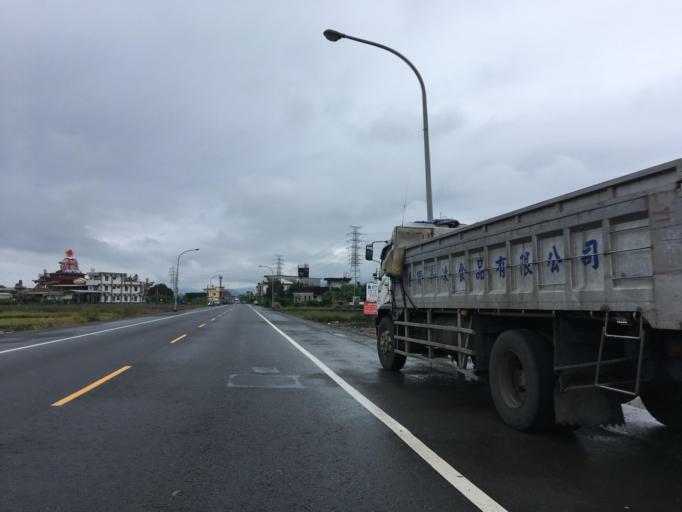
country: TW
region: Taiwan
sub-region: Yilan
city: Yilan
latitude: 24.6630
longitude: 121.7516
